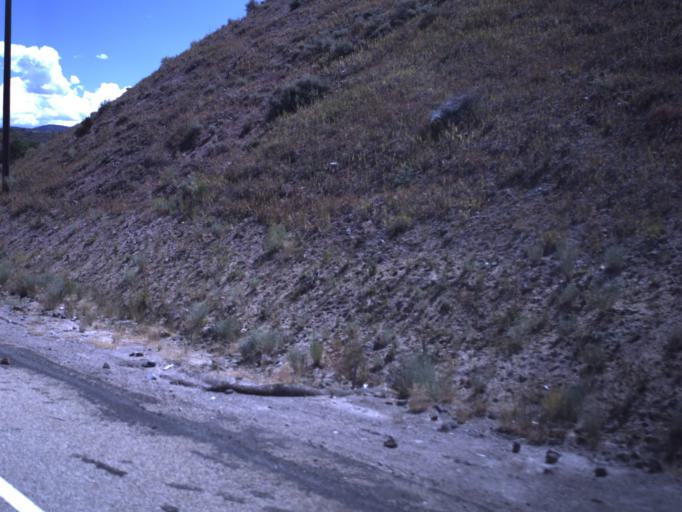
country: US
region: Utah
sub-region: Summit County
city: Francis
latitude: 40.6011
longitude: -111.3360
